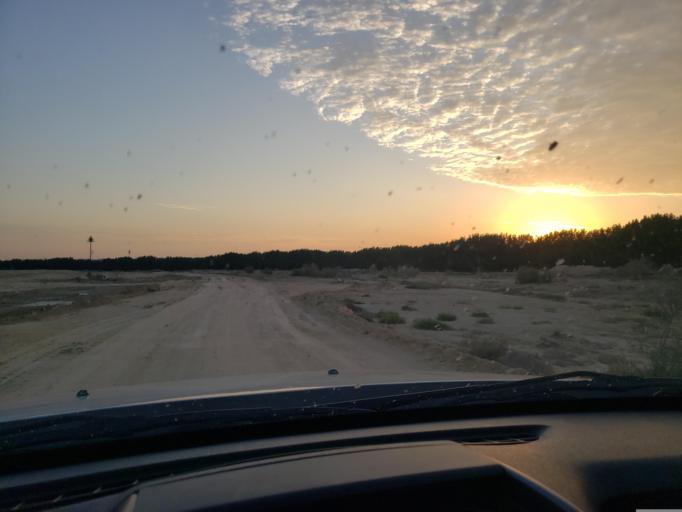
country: AE
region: Dubai
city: Dubai
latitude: 25.0200
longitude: 55.2630
